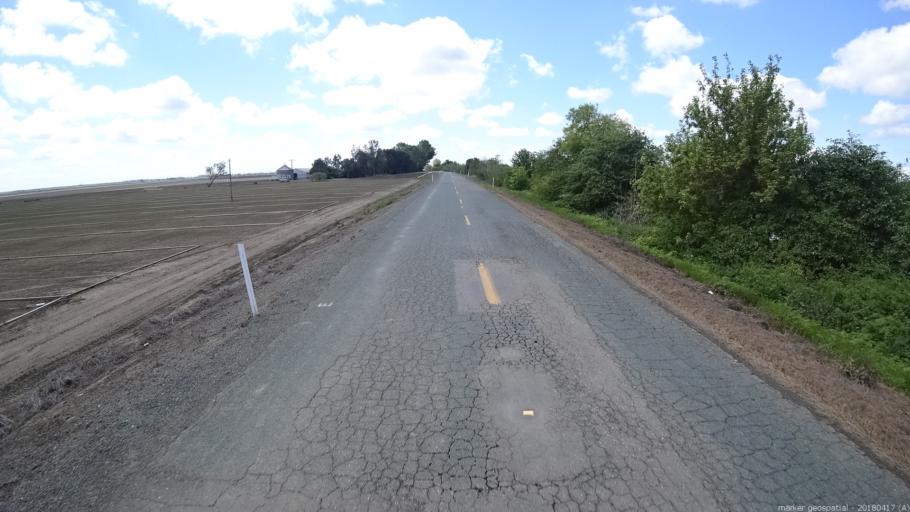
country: US
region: California
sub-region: Sacramento County
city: Walnut Grove
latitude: 38.1944
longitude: -121.5489
